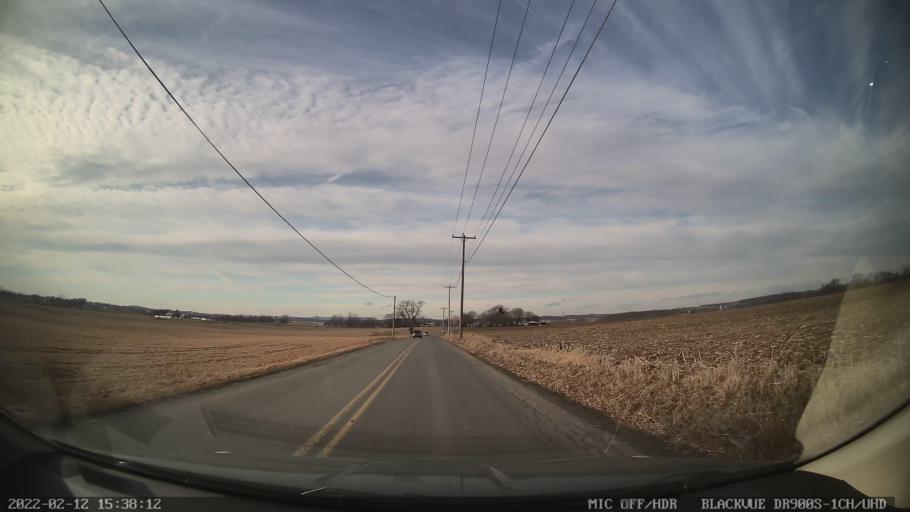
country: US
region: Pennsylvania
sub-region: Berks County
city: Topton
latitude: 40.5030
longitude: -75.7315
